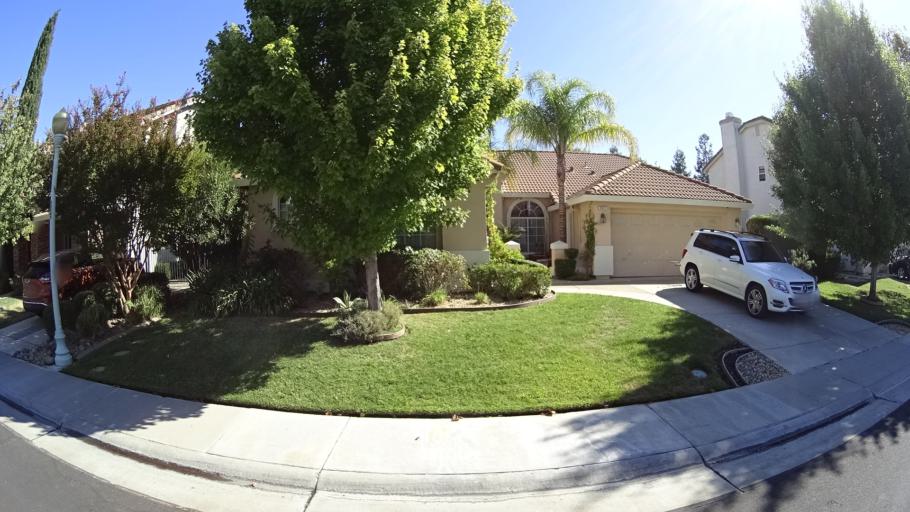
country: US
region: California
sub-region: Sacramento County
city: Laguna
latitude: 38.4186
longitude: -121.4803
